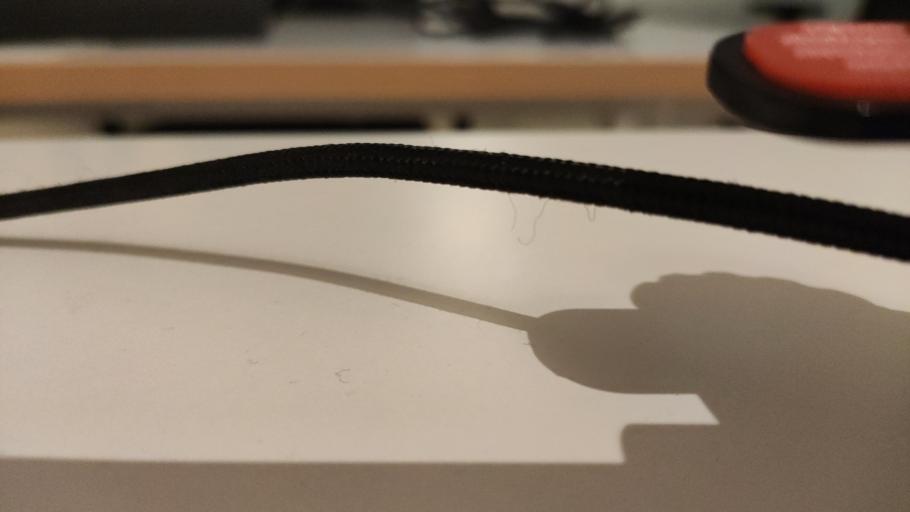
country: RU
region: Moskovskaya
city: Shaburnovo
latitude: 56.4344
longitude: 37.9271
